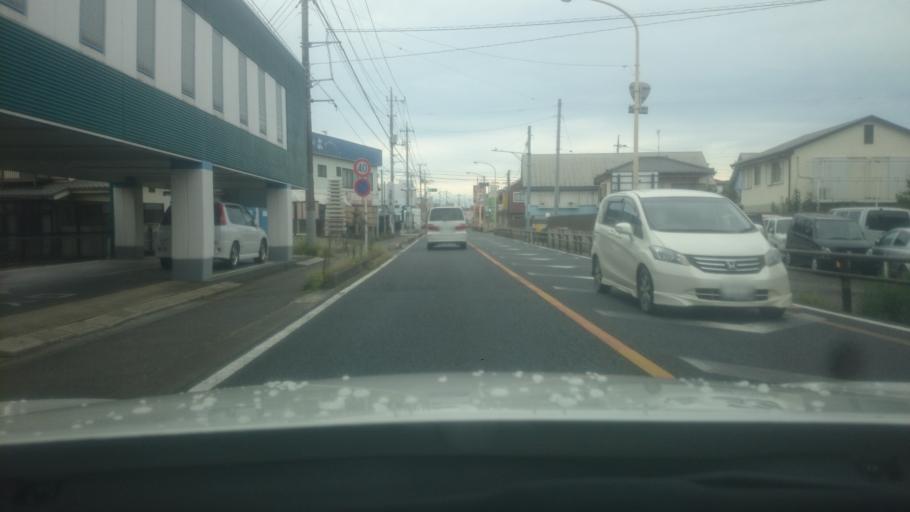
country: JP
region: Saitama
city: Kamifukuoka
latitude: 35.8764
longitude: 139.5010
